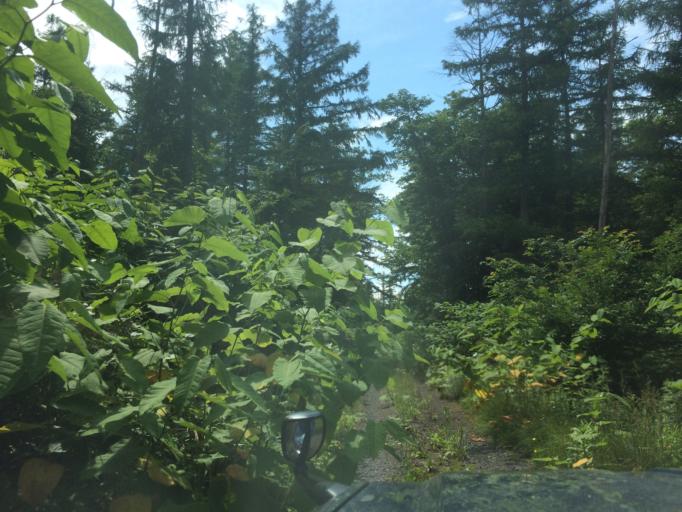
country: JP
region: Hokkaido
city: Niseko Town
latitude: 42.8652
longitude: 140.7995
